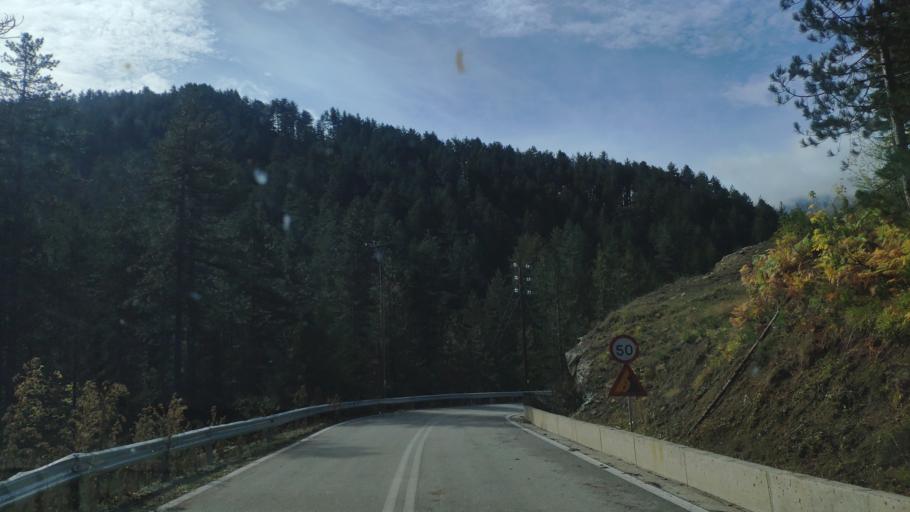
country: AL
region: Korce
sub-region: Rrethi i Devollit
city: Miras
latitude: 40.3991
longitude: 20.8960
